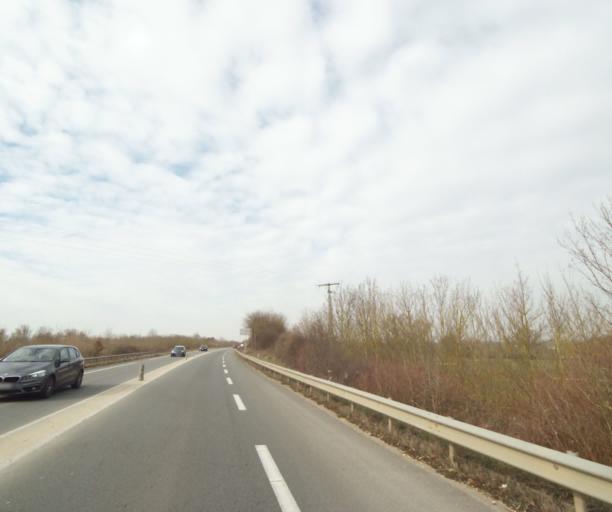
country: FR
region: Poitou-Charentes
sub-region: Departement des Deux-Sevres
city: Aiffres
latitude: 46.2944
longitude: -0.4505
